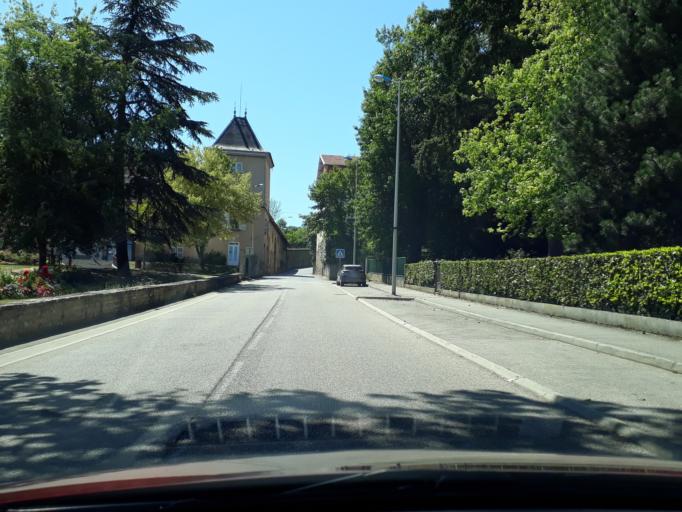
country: FR
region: Rhone-Alpes
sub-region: Departement du Rhone
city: Saint-Bonnet-de-Mure
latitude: 45.6914
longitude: 5.0286
